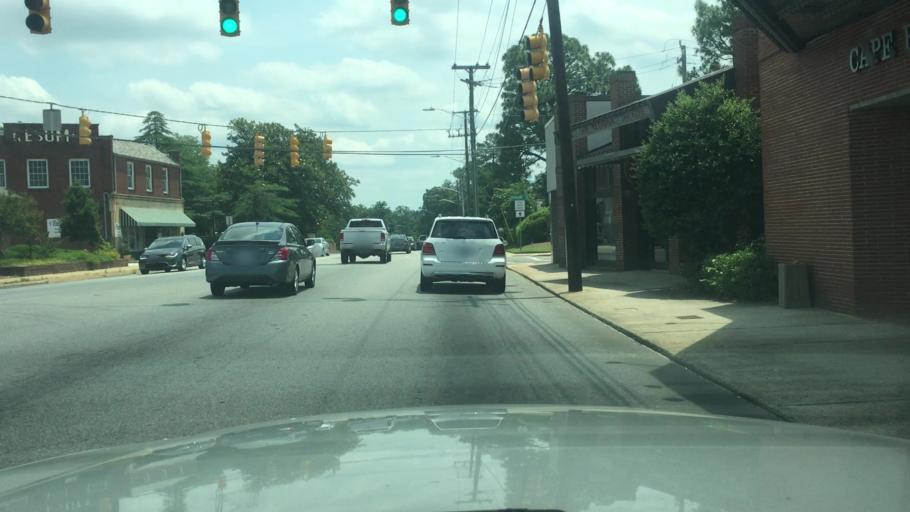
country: US
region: North Carolina
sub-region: Cumberland County
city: Fayetteville
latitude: 35.0567
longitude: -78.8994
